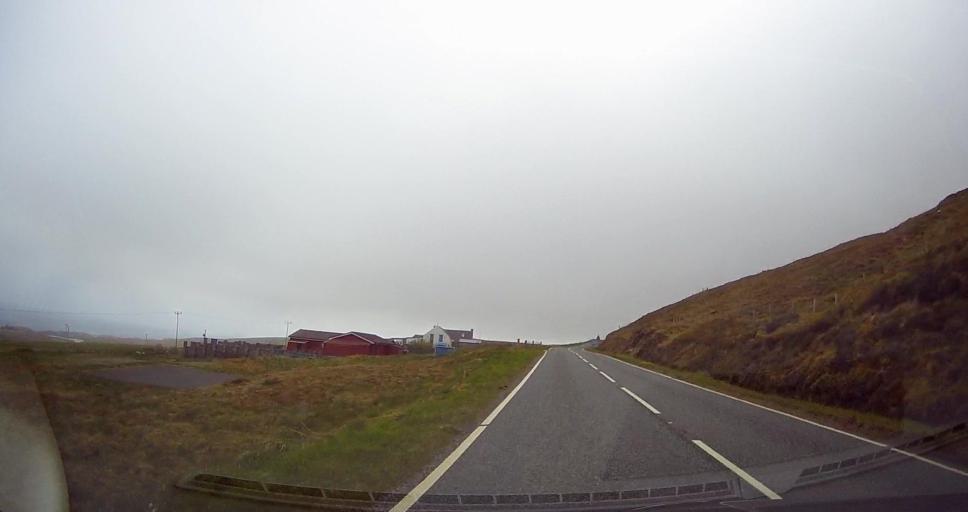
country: GB
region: Scotland
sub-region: Shetland Islands
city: Sandwick
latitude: 59.9737
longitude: -1.2771
